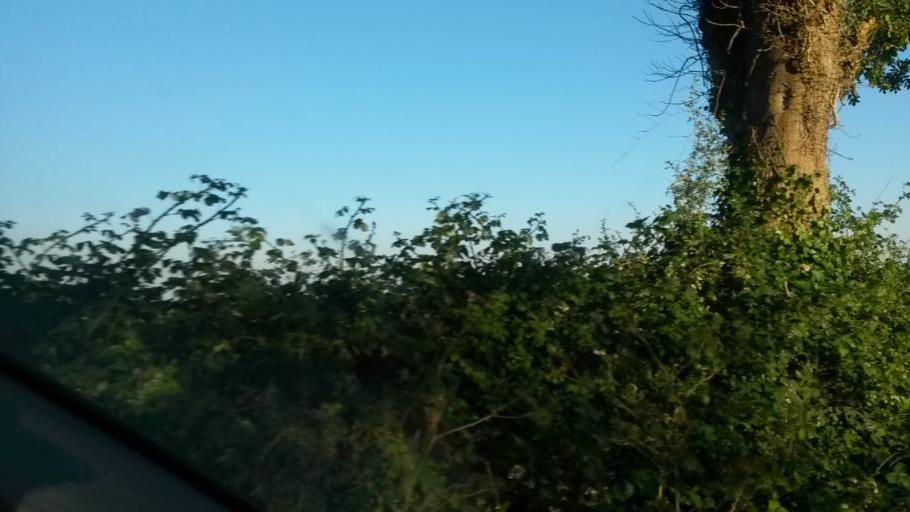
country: IE
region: Leinster
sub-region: An Mhi
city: Ashbourne
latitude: 53.5467
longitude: -6.3595
